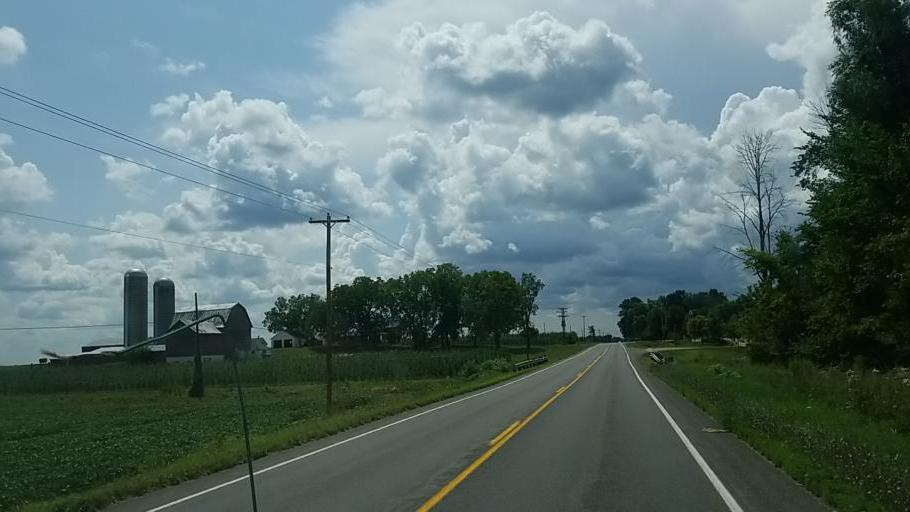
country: US
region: Michigan
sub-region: Kent County
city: Sparta
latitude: 43.1129
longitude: -85.7686
